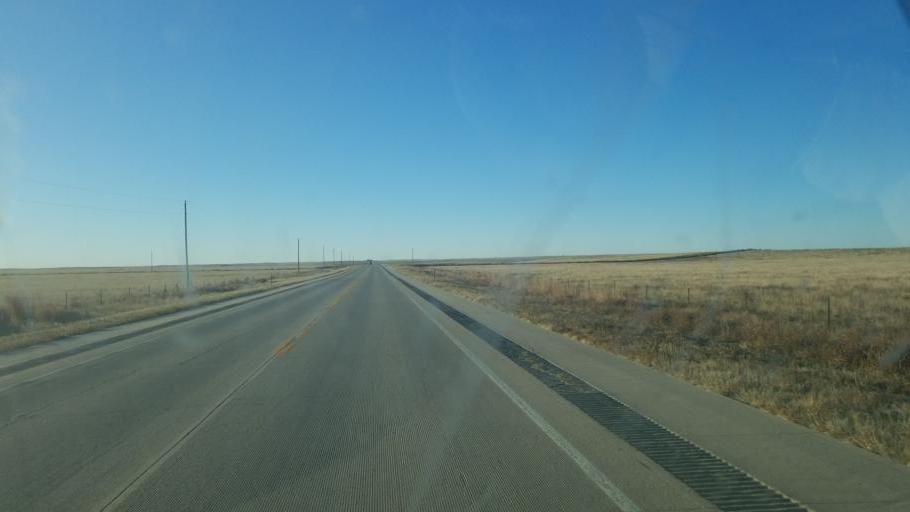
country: US
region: Colorado
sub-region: Kiowa County
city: Eads
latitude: 38.6465
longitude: -102.7860
